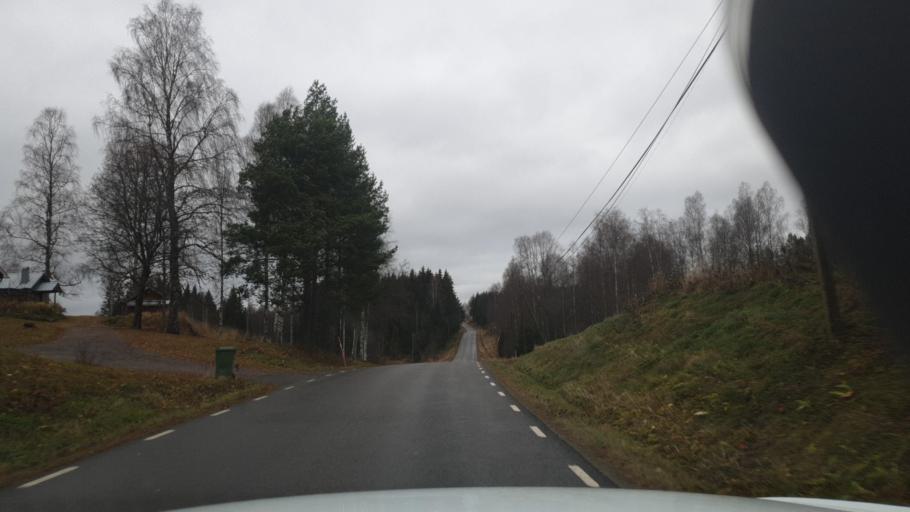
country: SE
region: Vaermland
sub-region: Eda Kommun
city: Amotfors
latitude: 59.9167
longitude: 12.5203
